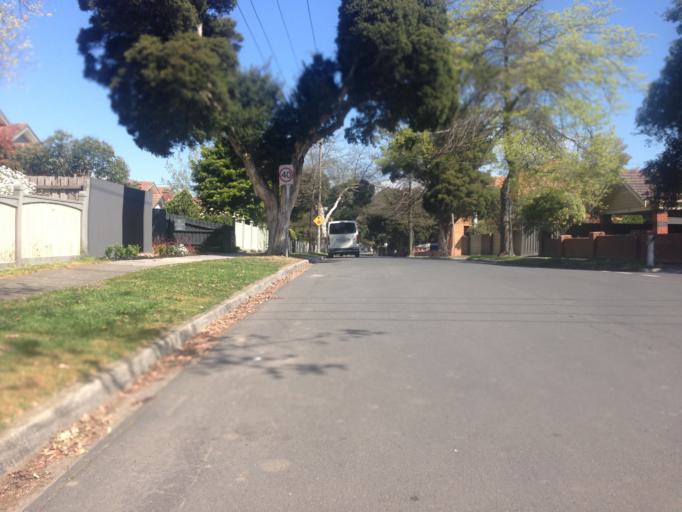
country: AU
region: Victoria
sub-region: Boroondara
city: Kew East
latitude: -37.7947
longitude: 145.0505
